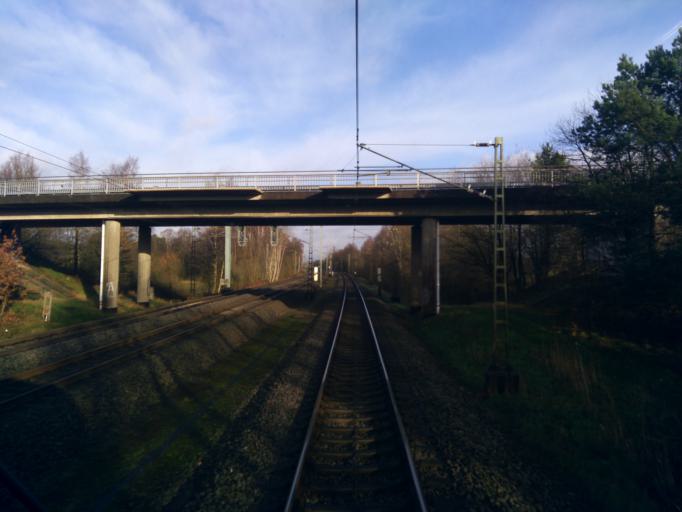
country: DE
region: Lower Saxony
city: Scheessel
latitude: 53.1429
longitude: 9.4657
